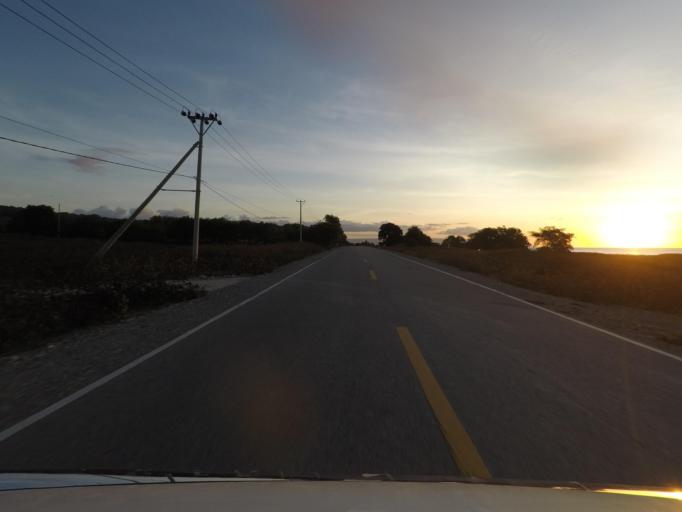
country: TL
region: Baucau
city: Baucau
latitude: -8.4537
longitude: 126.6288
